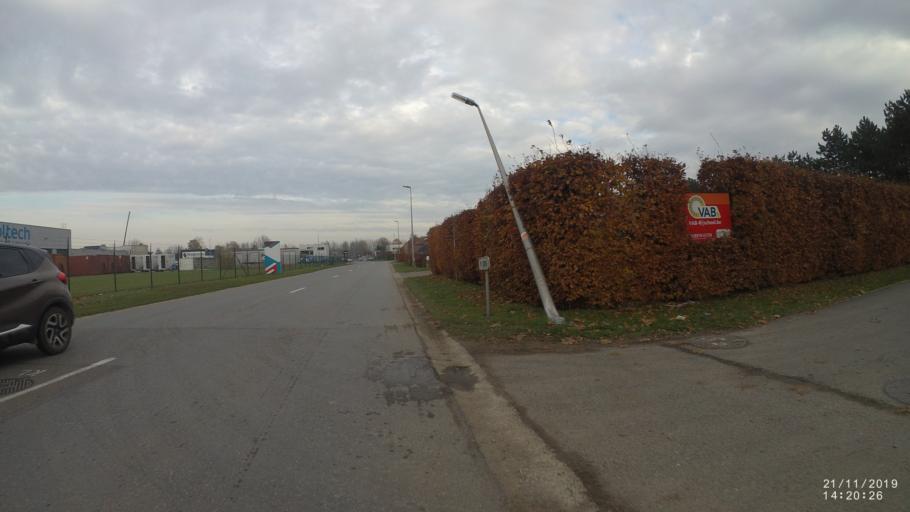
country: BE
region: Flanders
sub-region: Provincie Limburg
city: Alken
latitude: 50.8893
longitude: 5.3024
